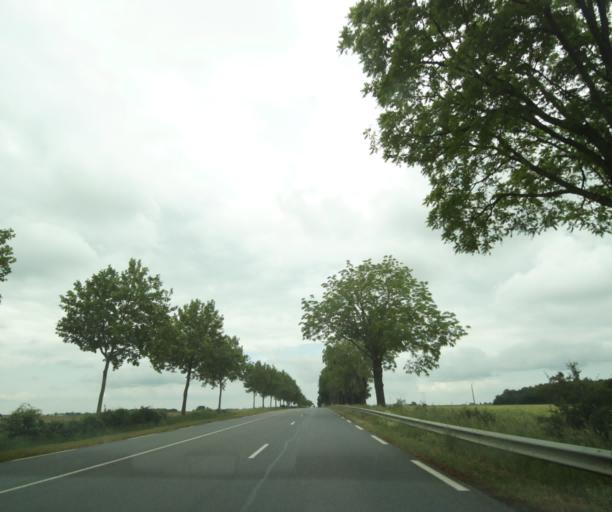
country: FR
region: Poitou-Charentes
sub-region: Departement des Deux-Sevres
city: Saint-Jean-de-Thouars
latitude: 46.9387
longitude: -0.2022
